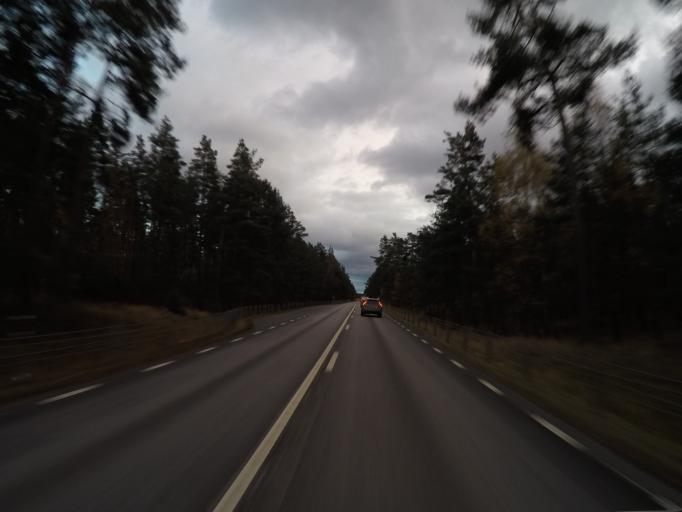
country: SE
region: Skane
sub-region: Kristianstads Kommun
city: Degeberga
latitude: 55.8573
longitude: 14.0920
